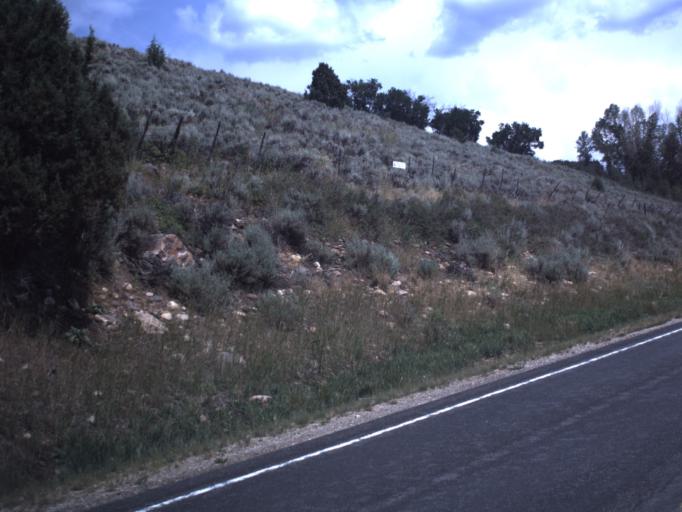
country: US
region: Utah
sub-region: Summit County
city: Francis
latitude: 40.5539
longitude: -111.1494
